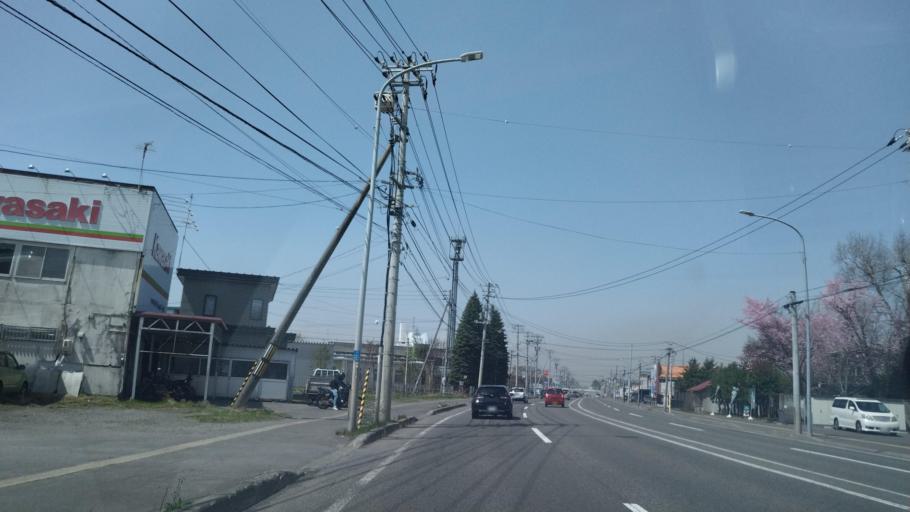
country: JP
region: Hokkaido
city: Obihiro
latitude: 42.9269
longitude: 143.2221
